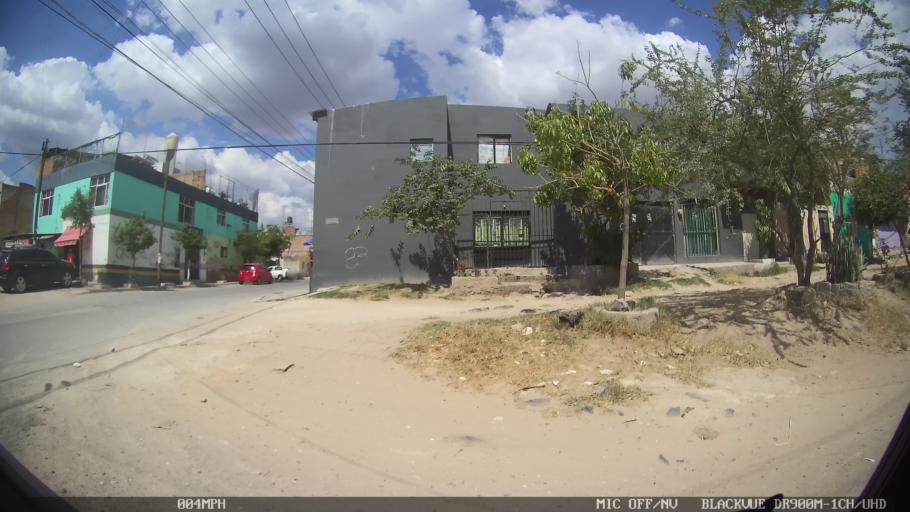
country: MX
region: Jalisco
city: Tlaquepaque
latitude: 20.6875
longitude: -103.2674
